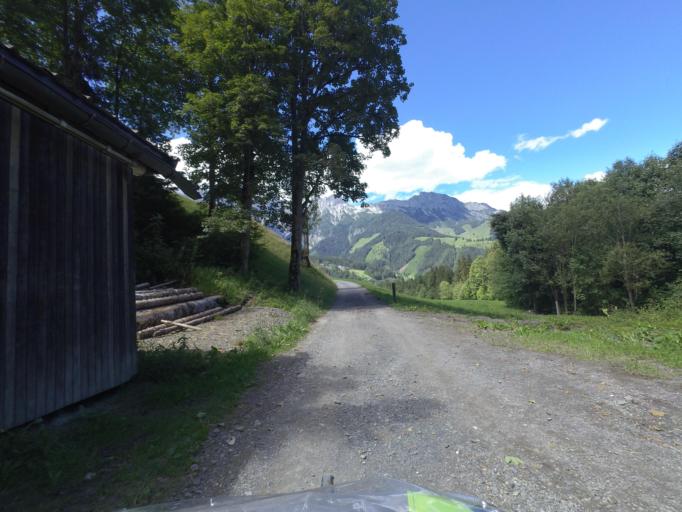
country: AT
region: Salzburg
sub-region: Politischer Bezirk Zell am See
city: Leogang
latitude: 47.4307
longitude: 12.7660
